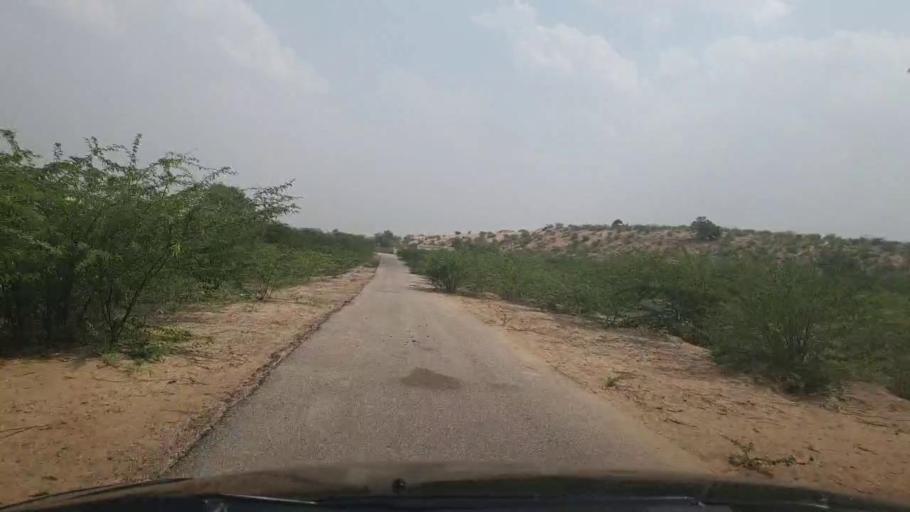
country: PK
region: Sindh
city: Islamkot
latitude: 25.0290
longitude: 70.5462
